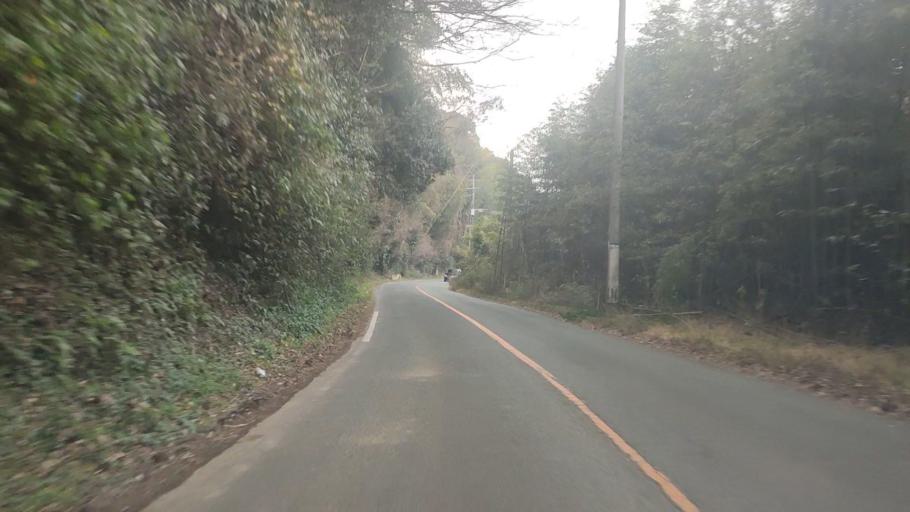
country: JP
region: Kumamoto
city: Ozu
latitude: 32.8531
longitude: 130.8620
